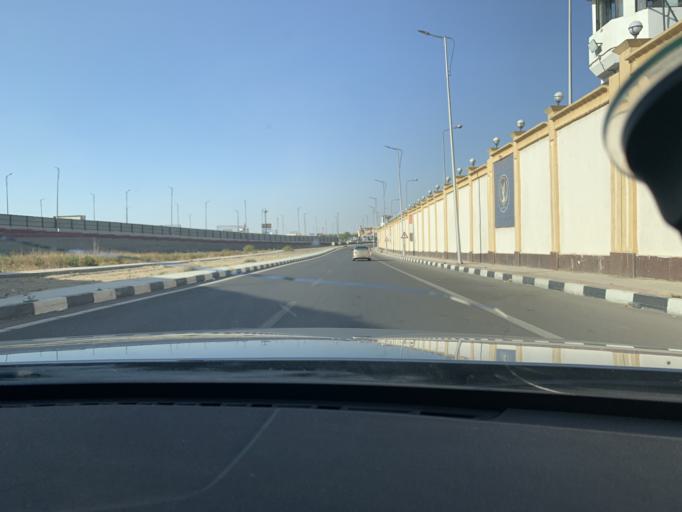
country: EG
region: Muhafazat al Qahirah
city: Cairo
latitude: 30.0516
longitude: 31.4112
